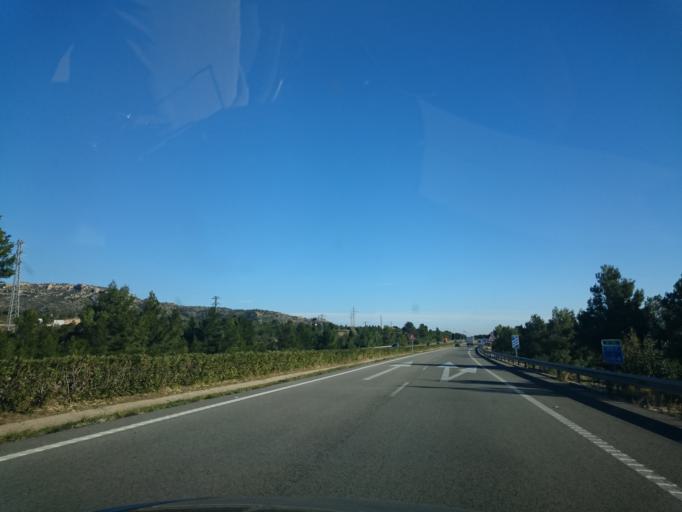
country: ES
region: Catalonia
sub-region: Provincia de Tarragona
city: Colldejou
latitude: 40.9817
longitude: 0.8882
